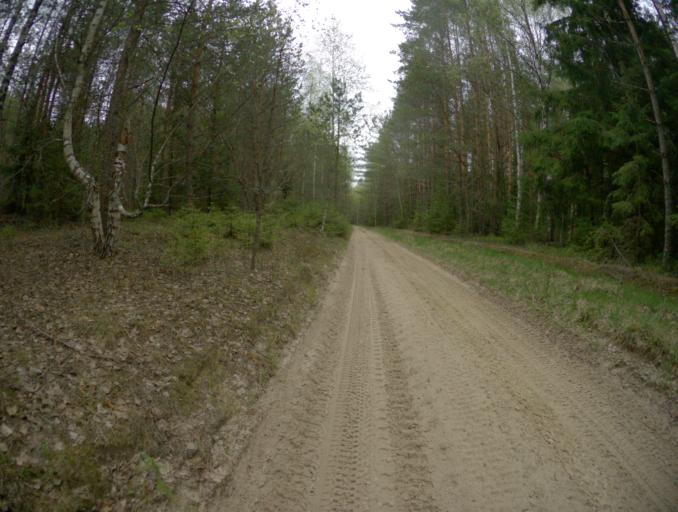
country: RU
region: Vladimir
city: Golovino
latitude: 55.8937
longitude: 40.4159
